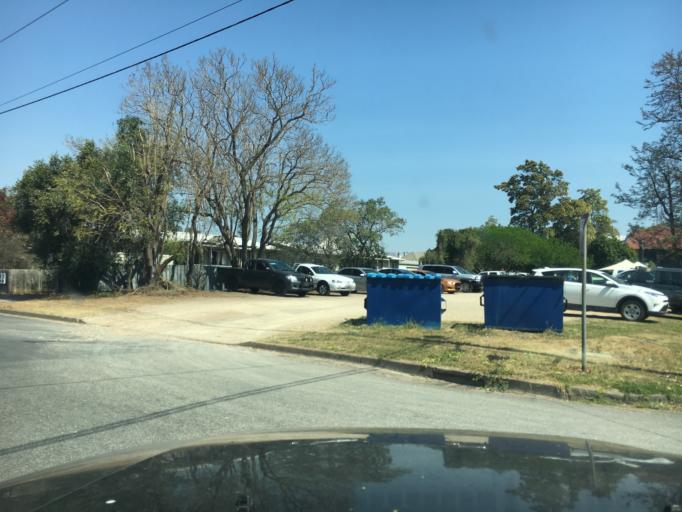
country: AU
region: New South Wales
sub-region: Singleton
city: Singleton
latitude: -32.5605
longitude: 151.1757
